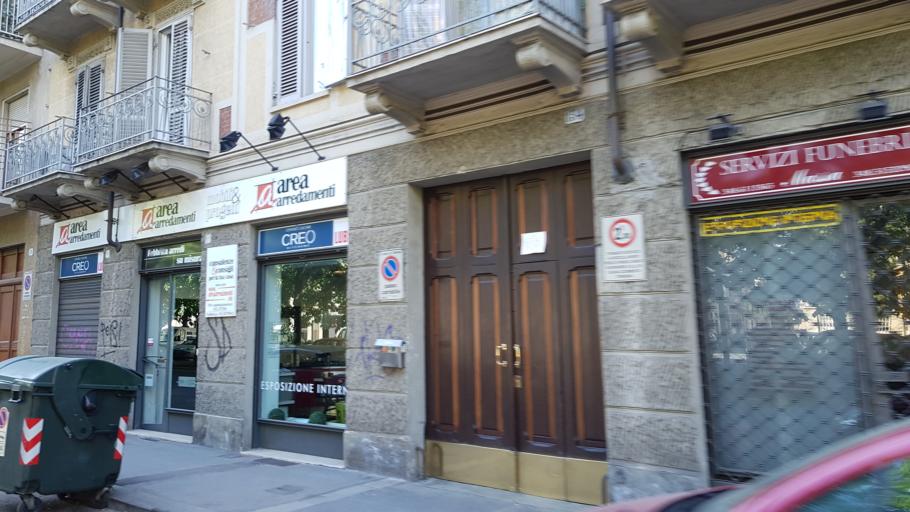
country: IT
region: Piedmont
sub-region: Provincia di Torino
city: Lesna
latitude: 45.0631
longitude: 7.6449
